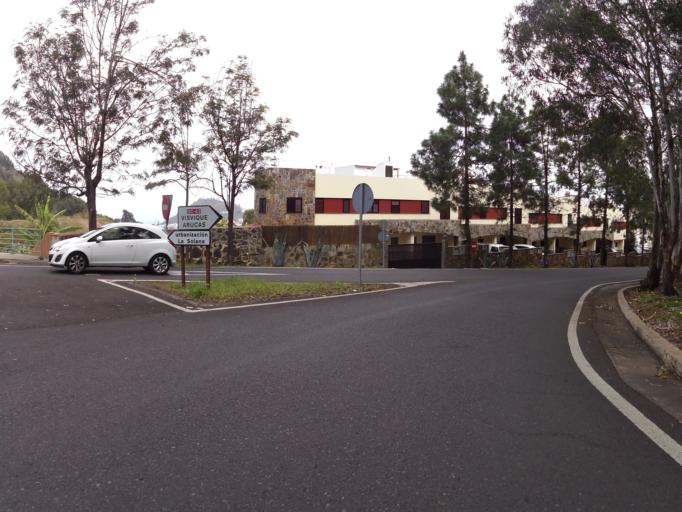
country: ES
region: Canary Islands
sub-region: Provincia de Las Palmas
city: Arucas
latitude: 28.1020
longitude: -15.5312
